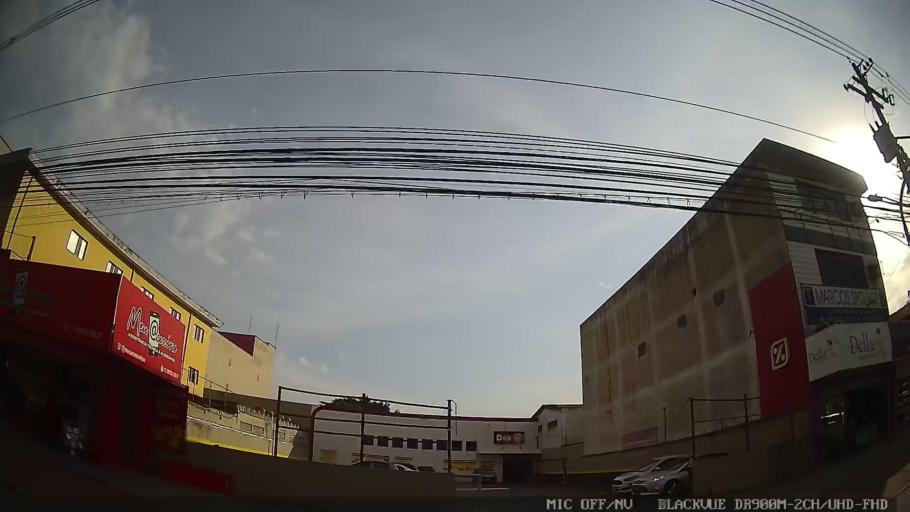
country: BR
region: Sao Paulo
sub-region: Cubatao
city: Cubatao
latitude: -23.8883
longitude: -46.4198
